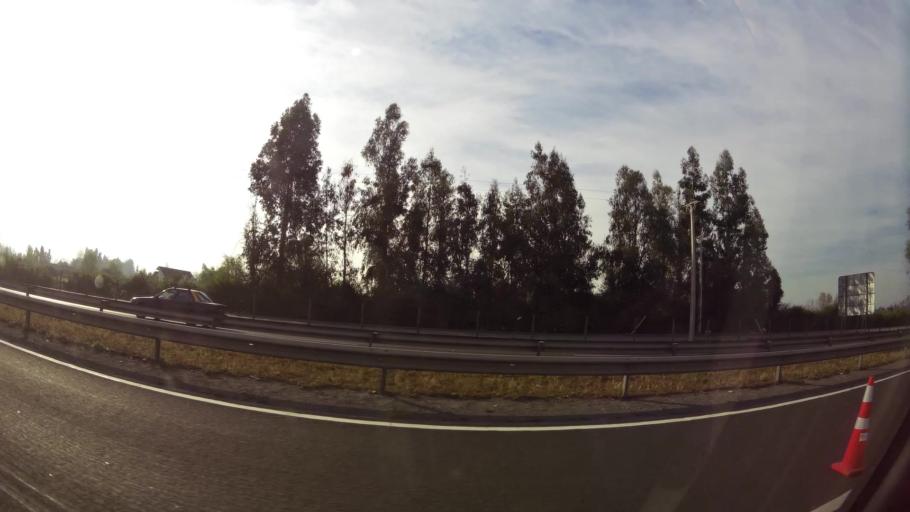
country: CL
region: Santiago Metropolitan
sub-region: Provincia de Talagante
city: Penaflor
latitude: -33.6172
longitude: -70.8565
